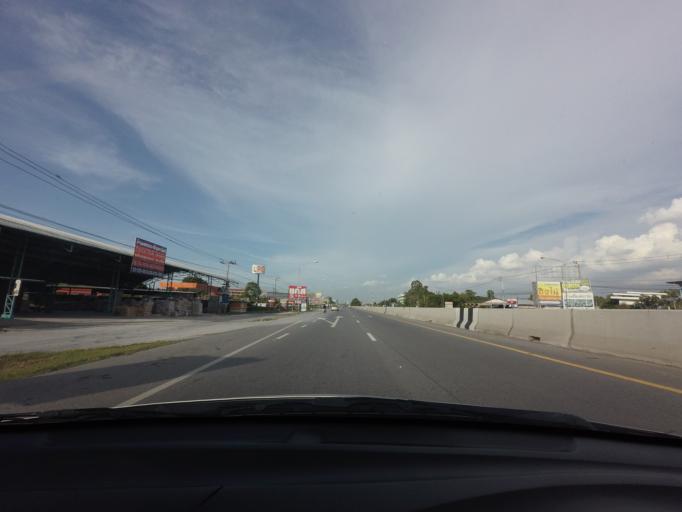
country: TH
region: Nonthaburi
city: Bang Bua Thong
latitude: 13.9475
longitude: 100.4394
